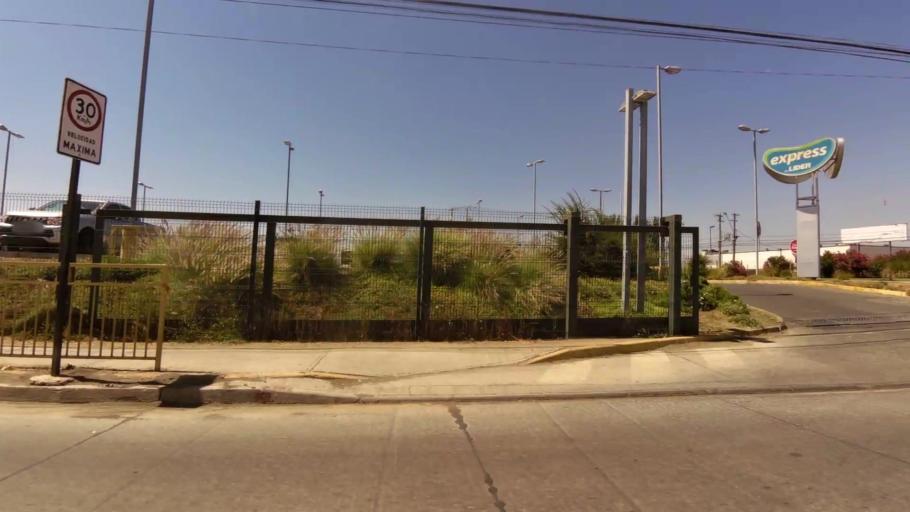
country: CL
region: Maule
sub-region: Provincia de Curico
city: Curico
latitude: -34.9747
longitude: -71.2212
